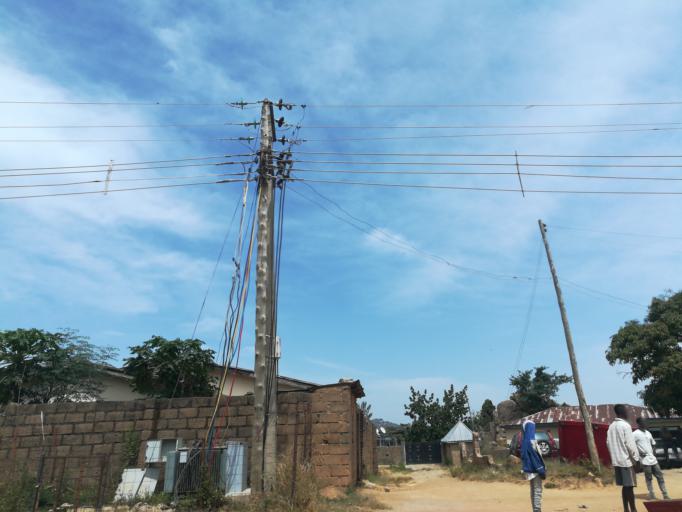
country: NG
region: Plateau
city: Jos
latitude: 9.9270
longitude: 8.8444
